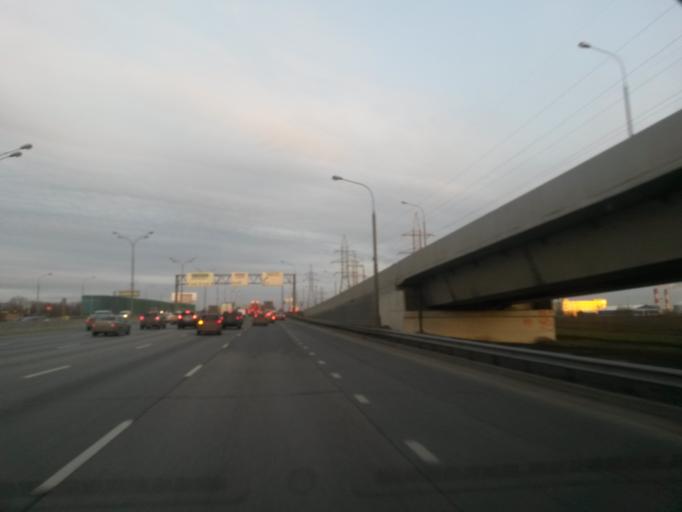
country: RU
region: Moscow
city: Mikhalkovo
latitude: 55.6646
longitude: 37.4307
